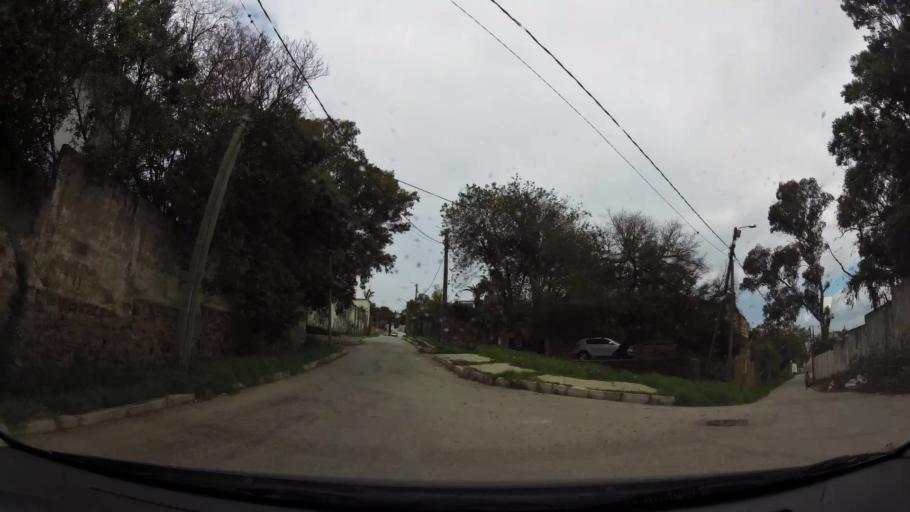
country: MA
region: Tanger-Tetouan
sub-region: Tanger-Assilah
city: Tangier
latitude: 35.7831
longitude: -5.8501
